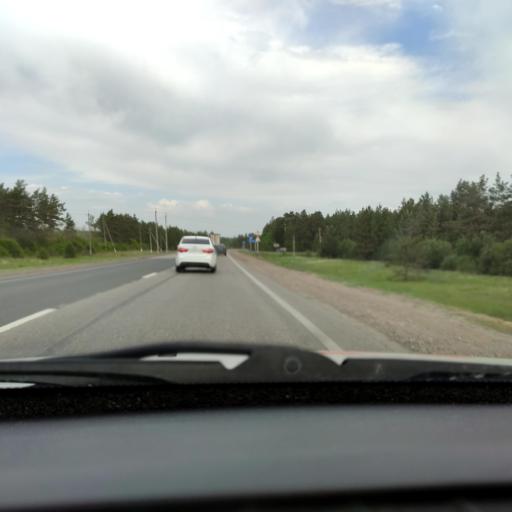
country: RU
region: Samara
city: Mirnyy
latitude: 53.5275
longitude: 50.3107
